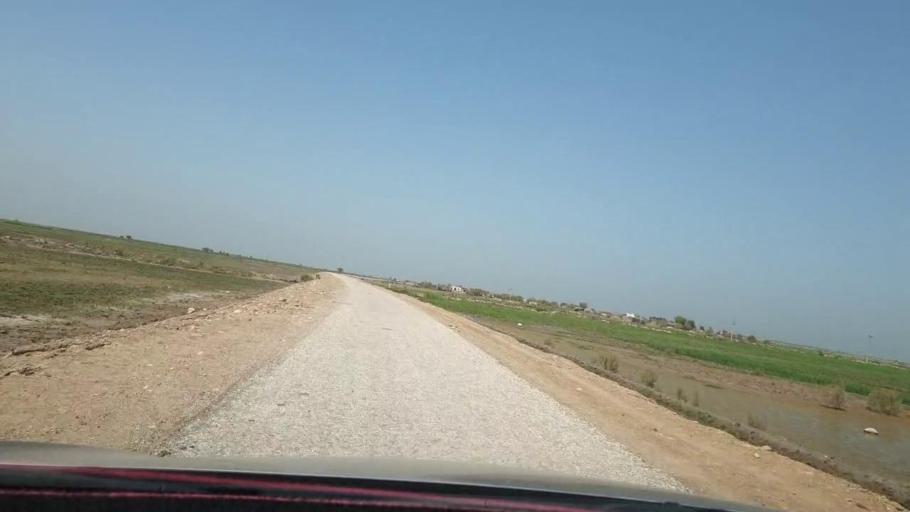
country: PK
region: Sindh
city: Warah
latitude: 27.5644
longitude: 67.7545
